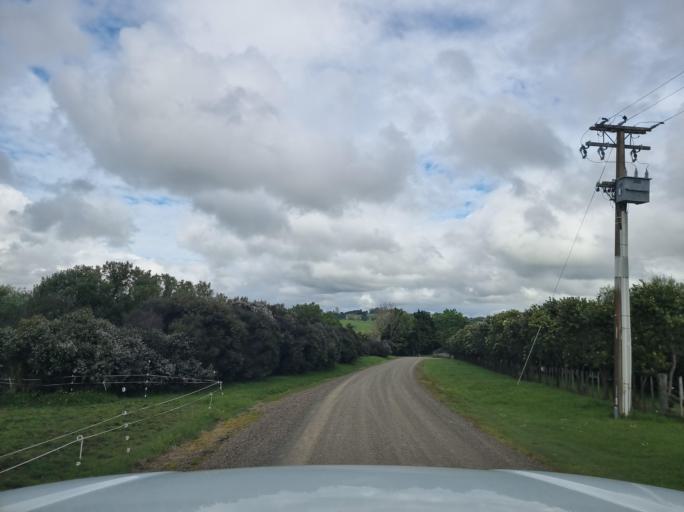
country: NZ
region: Northland
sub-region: Whangarei
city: Ruakaka
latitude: -36.1275
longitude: 174.2046
